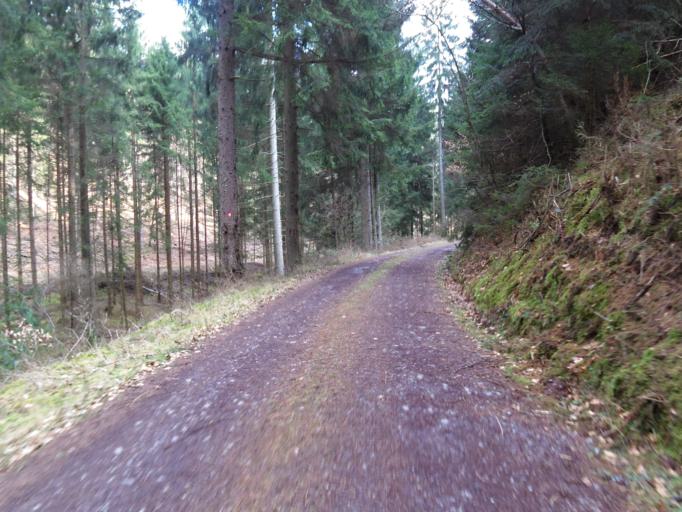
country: DE
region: Rheinland-Pfalz
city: Frankenstein
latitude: 49.4766
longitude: 8.0028
